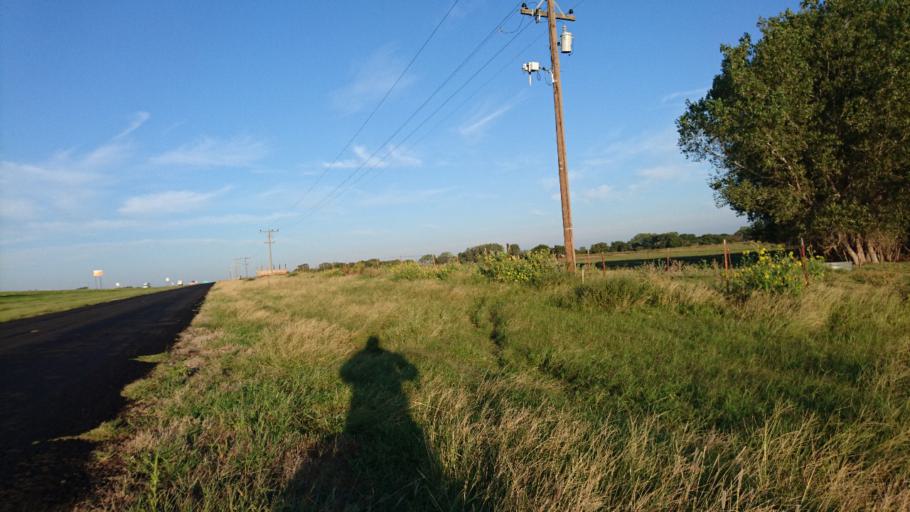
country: US
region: Oklahoma
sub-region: Beckham County
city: Sayre
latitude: 35.2625
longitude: -99.6924
